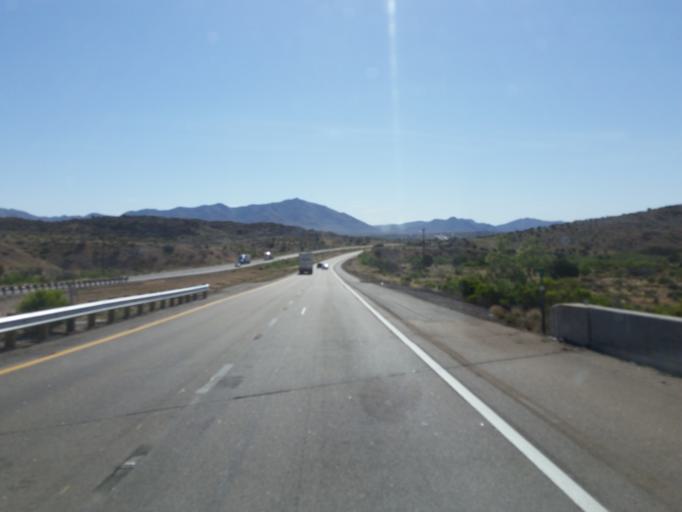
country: US
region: Arizona
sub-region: Mohave County
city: New Kingman-Butler
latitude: 35.1617
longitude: -113.6692
